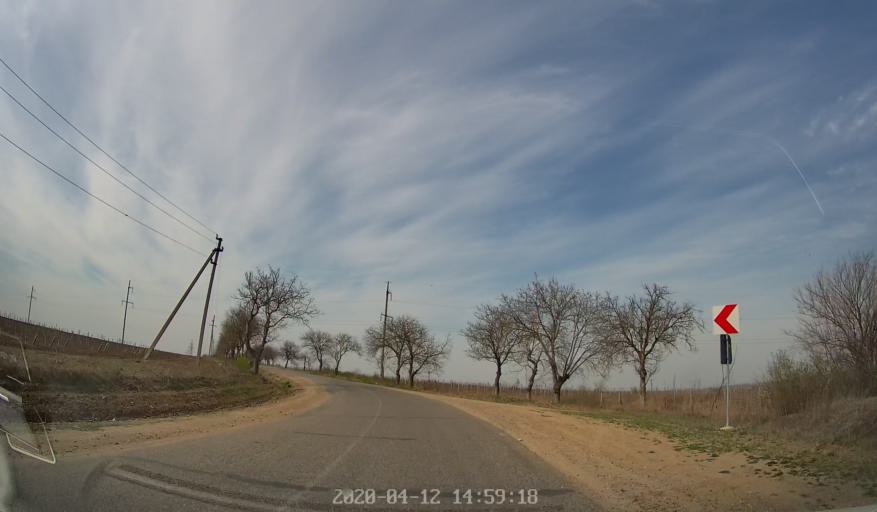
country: MD
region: Telenesti
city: Cocieri
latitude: 47.2698
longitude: 29.1140
